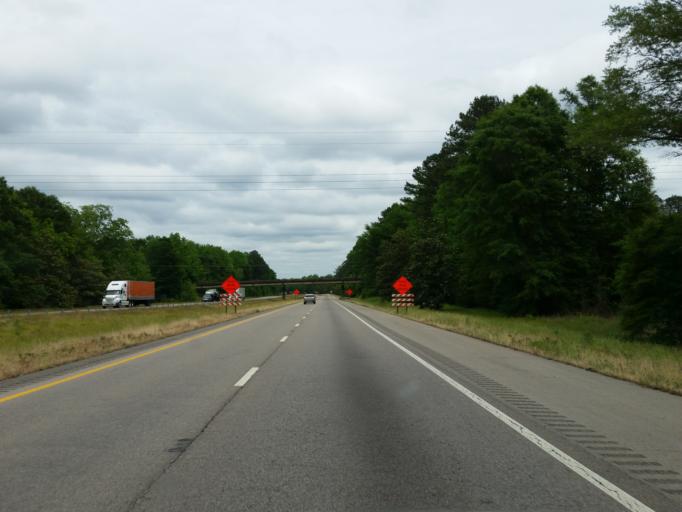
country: US
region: Mississippi
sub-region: Lauderdale County
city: Marion
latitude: 32.4109
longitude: -88.4723
